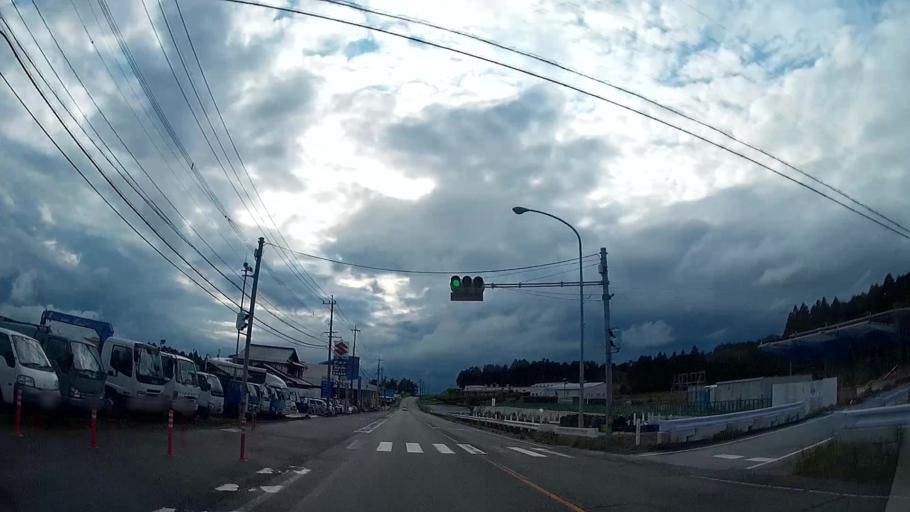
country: JP
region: Kumamoto
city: Ozu
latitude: 32.8773
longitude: 130.9202
